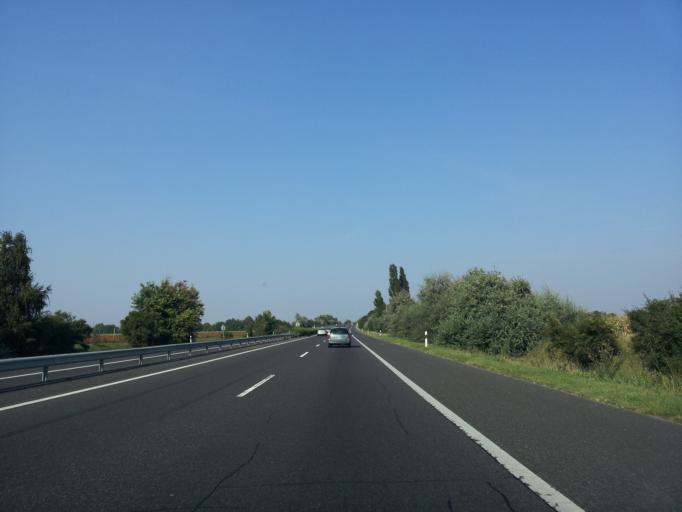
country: HU
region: Fejer
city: Szabadbattyan
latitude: 47.0745
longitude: 18.3488
